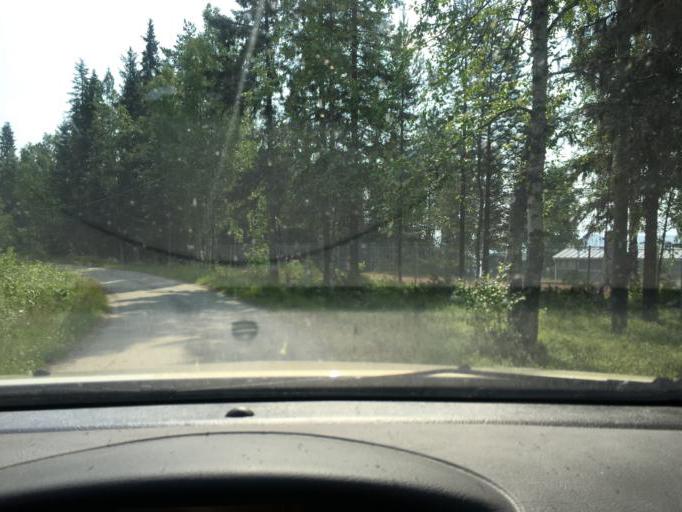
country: SE
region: Norrbotten
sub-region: Kalix Kommun
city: Rolfs
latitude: 65.7591
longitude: 22.9928
